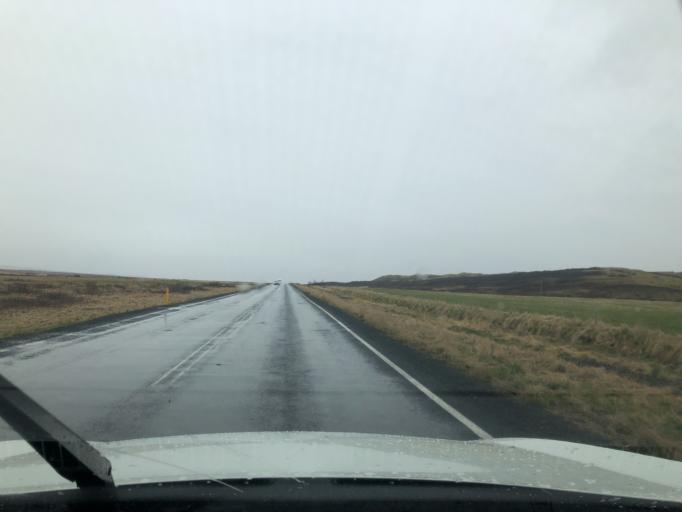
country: IS
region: South
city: Selfoss
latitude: 64.2992
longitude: -20.3319
